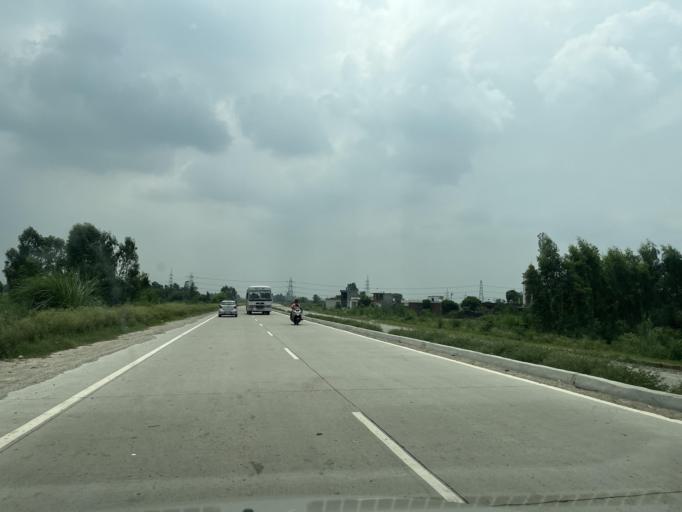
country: IN
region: Uttar Pradesh
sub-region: Bijnor
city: Najibabad
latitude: 29.5714
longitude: 78.3388
